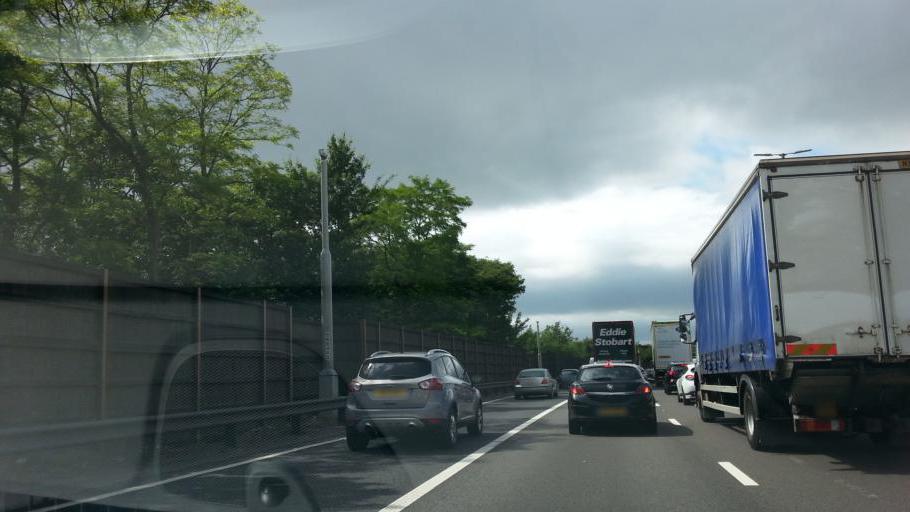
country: GB
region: England
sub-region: City and Borough of Birmingham
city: Hockley
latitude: 52.5278
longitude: -1.8946
